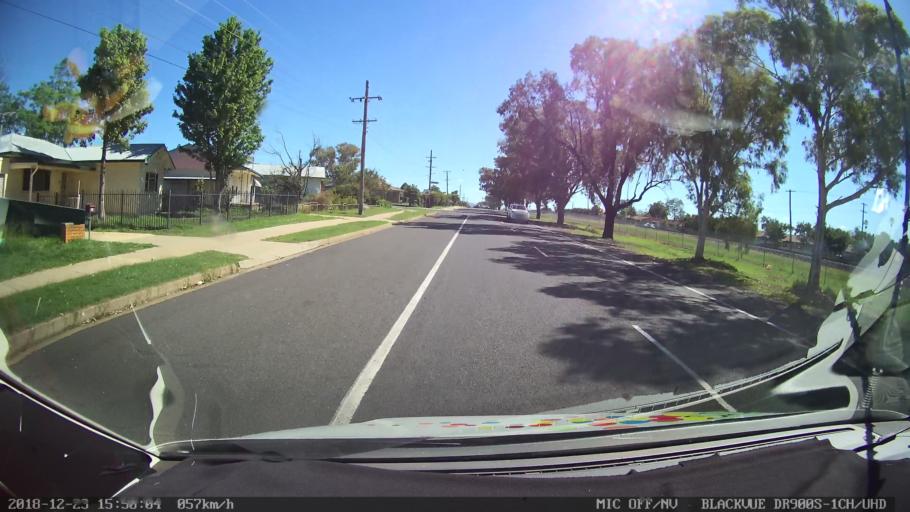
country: AU
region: New South Wales
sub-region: Tamworth Municipality
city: South Tamworth
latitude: -31.1036
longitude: 150.9026
